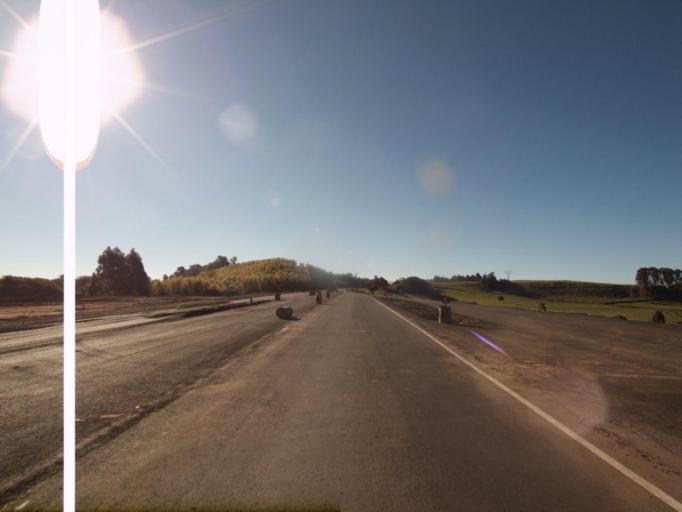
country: AR
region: Misiones
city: Bernardo de Irigoyen
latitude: -26.6377
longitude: -53.5185
